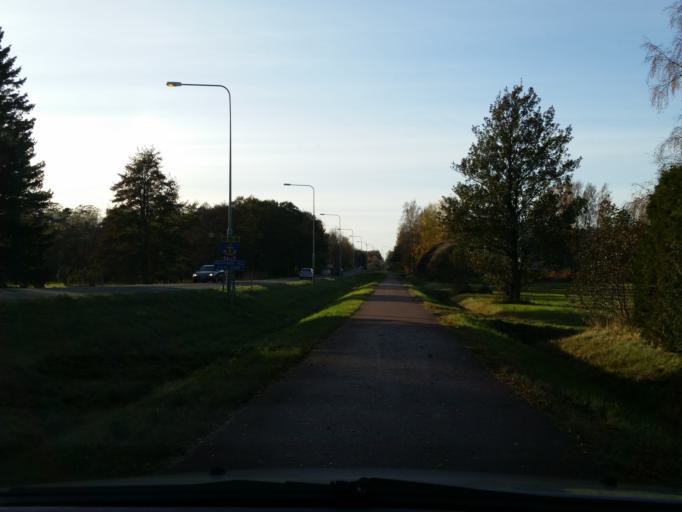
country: AX
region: Mariehamns stad
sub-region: Mariehamn
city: Mariehamn
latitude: 60.1158
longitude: 19.9572
